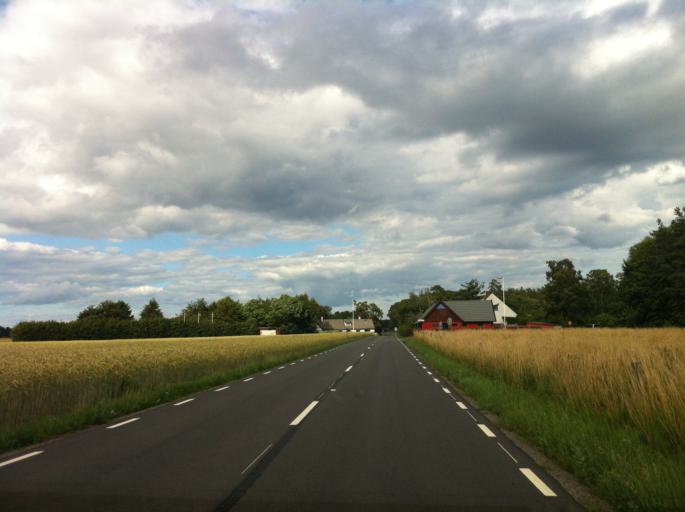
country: SE
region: Skane
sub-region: Simrishamns Kommun
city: Simrishamn
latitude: 55.3956
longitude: 14.1778
